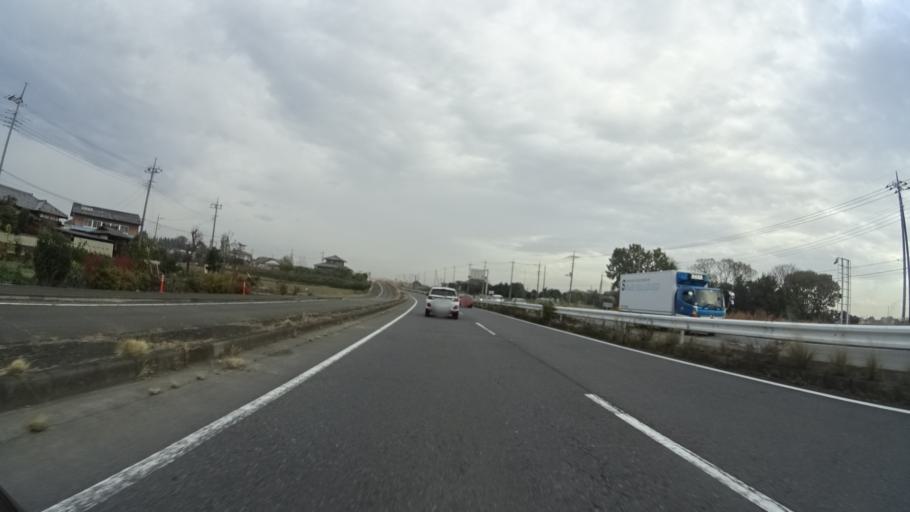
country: JP
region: Gunma
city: Isesaki
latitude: 36.3646
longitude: 139.1621
